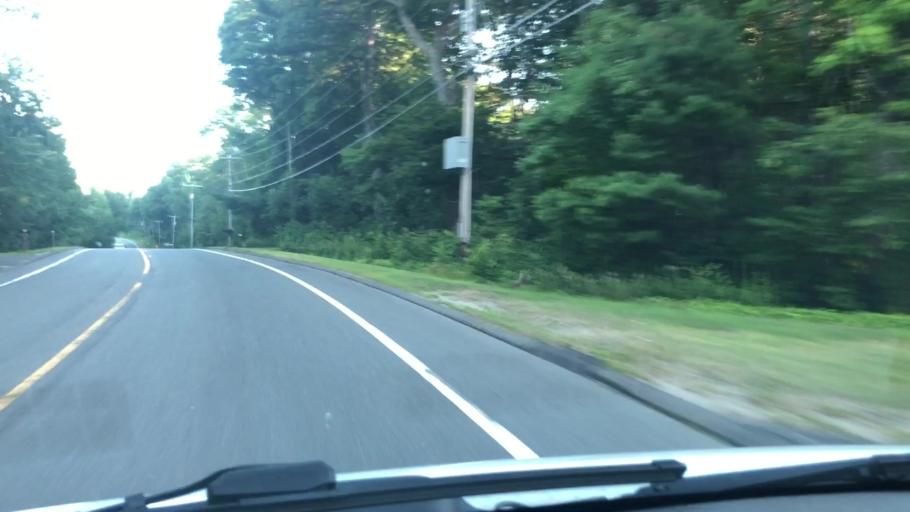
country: US
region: Massachusetts
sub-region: Hampshire County
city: Westhampton
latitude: 42.2858
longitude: -72.7975
